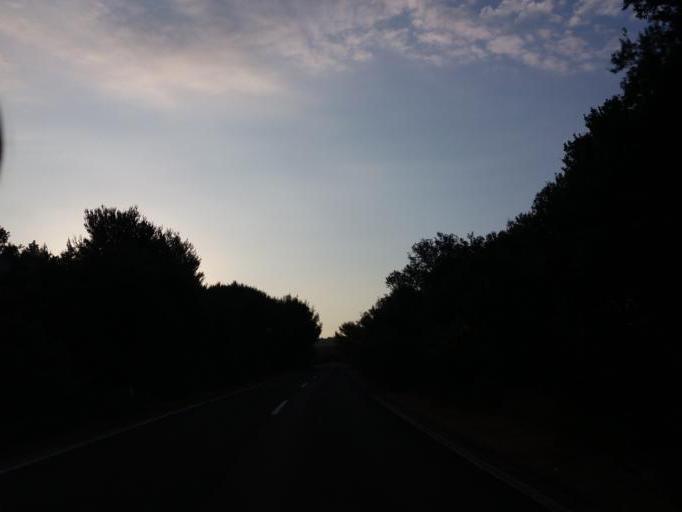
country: HR
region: Zadarska
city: Ugljan
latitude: 44.1358
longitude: 14.8680
